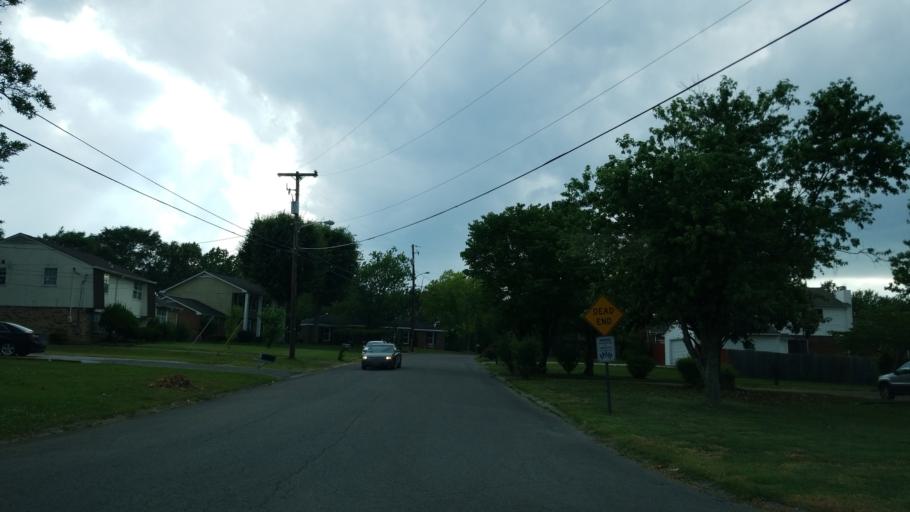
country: US
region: Tennessee
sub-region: Rutherford County
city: La Vergne
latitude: 36.0956
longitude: -86.6101
